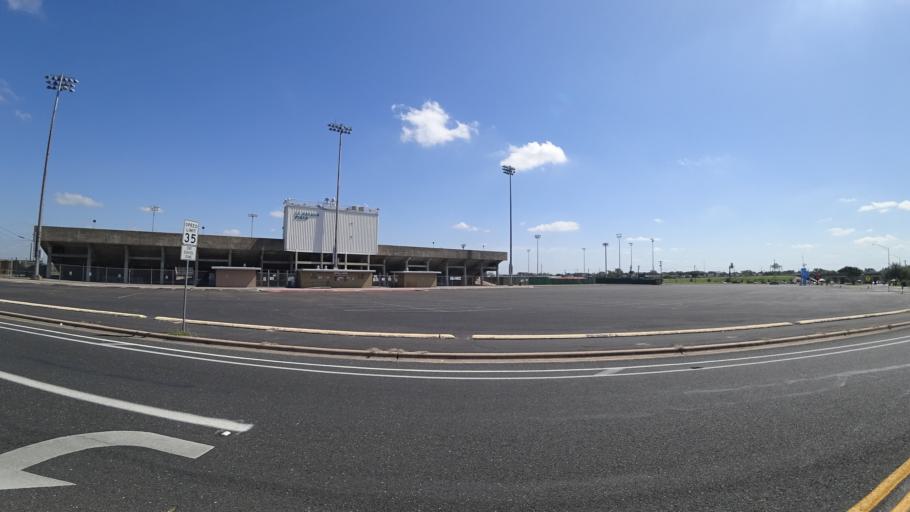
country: US
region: Texas
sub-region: Travis County
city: Austin
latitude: 30.3243
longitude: -97.6895
